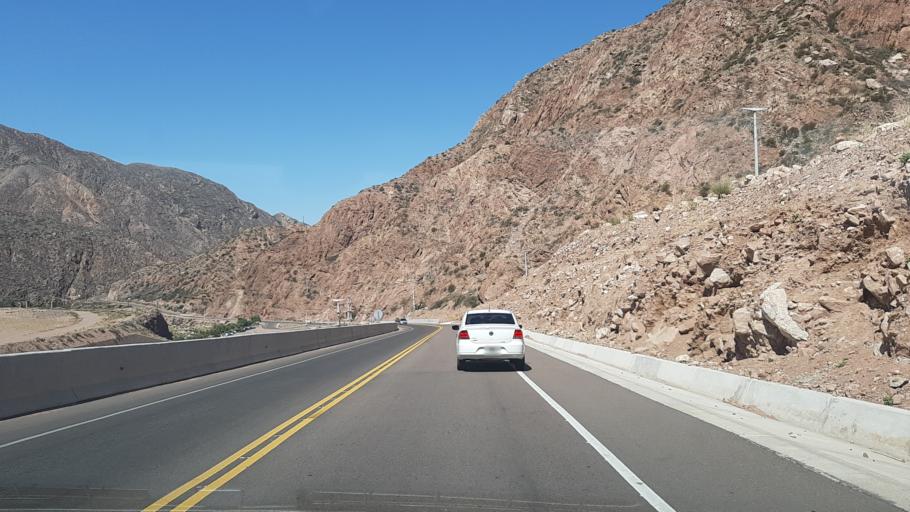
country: AR
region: Mendoza
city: Lujan de Cuyo
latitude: -33.0018
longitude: -69.1288
